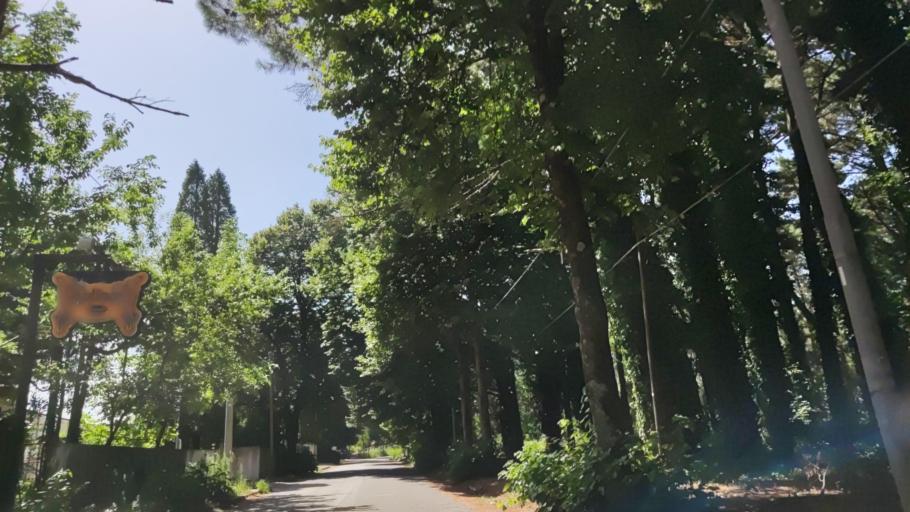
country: IT
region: Calabria
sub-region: Provincia di Reggio Calabria
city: Seminara
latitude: 38.3397
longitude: 15.8451
